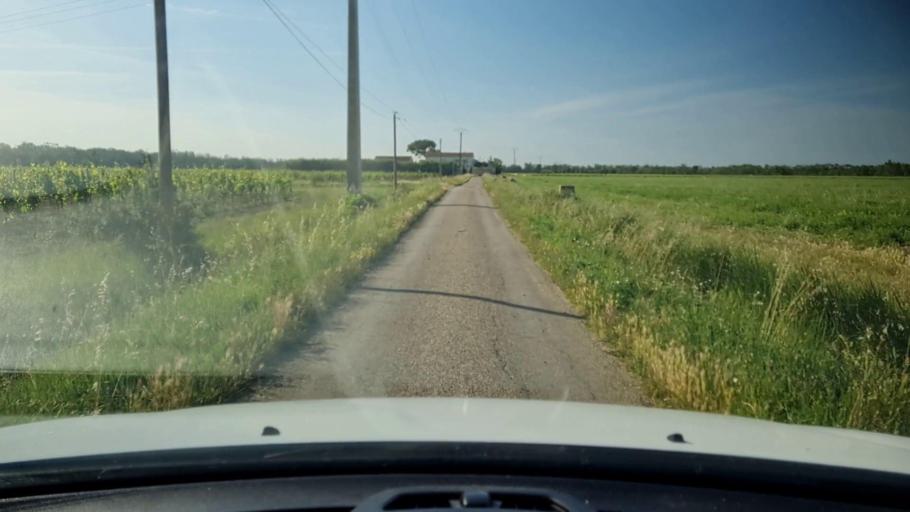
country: FR
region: Languedoc-Roussillon
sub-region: Departement du Gard
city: Le Cailar
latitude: 43.6411
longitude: 4.2290
